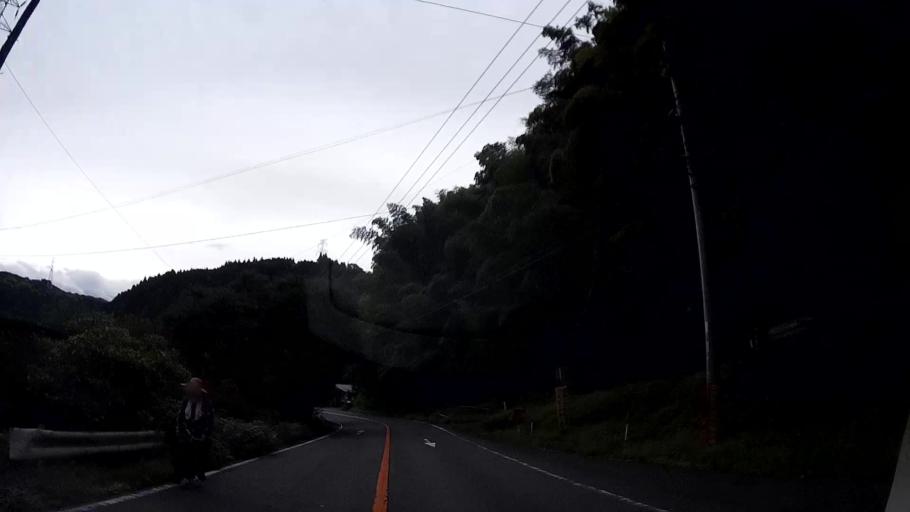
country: JP
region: Kumamoto
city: Kikuchi
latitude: 33.0137
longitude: 130.8845
